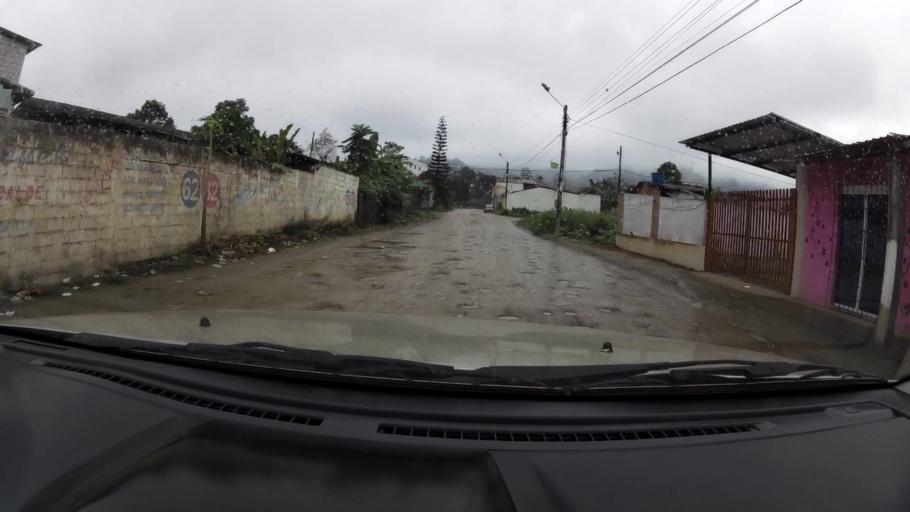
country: EC
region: Guayas
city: Balao
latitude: -3.0612
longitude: -79.7447
